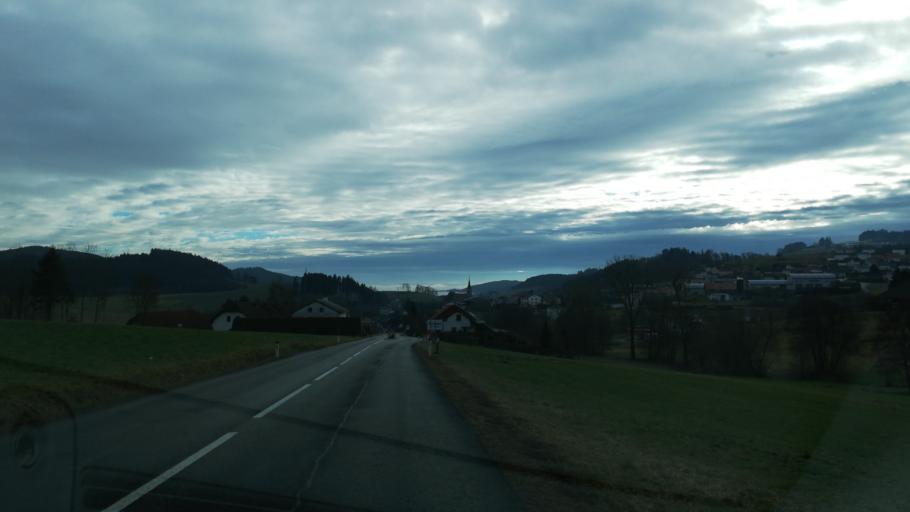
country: AT
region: Upper Austria
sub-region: Politischer Bezirk Urfahr-Umgebung
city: Reichenau im Muhlkreis
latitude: 48.4646
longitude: 14.3439
